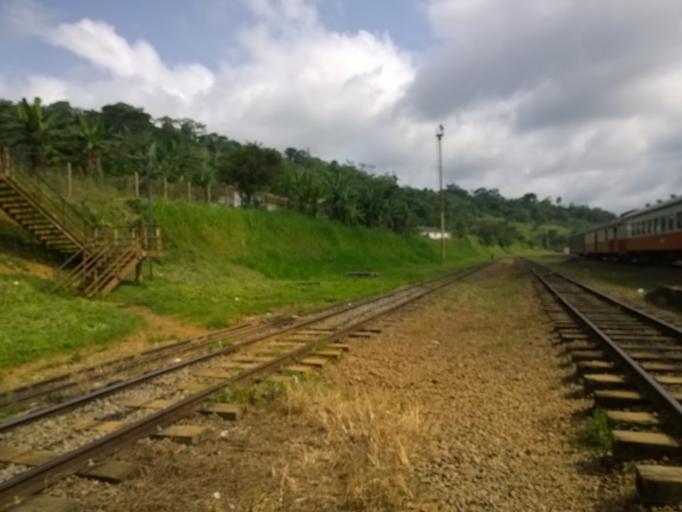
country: CM
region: Centre
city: Eseka
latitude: 3.6432
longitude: 10.7722
